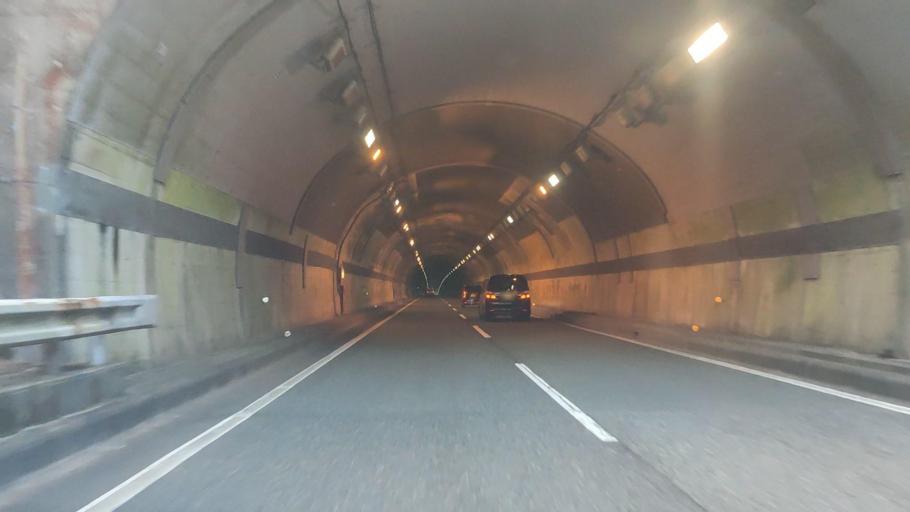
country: JP
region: Yamaguchi
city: Shimonoseki
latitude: 33.9204
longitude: 130.9683
